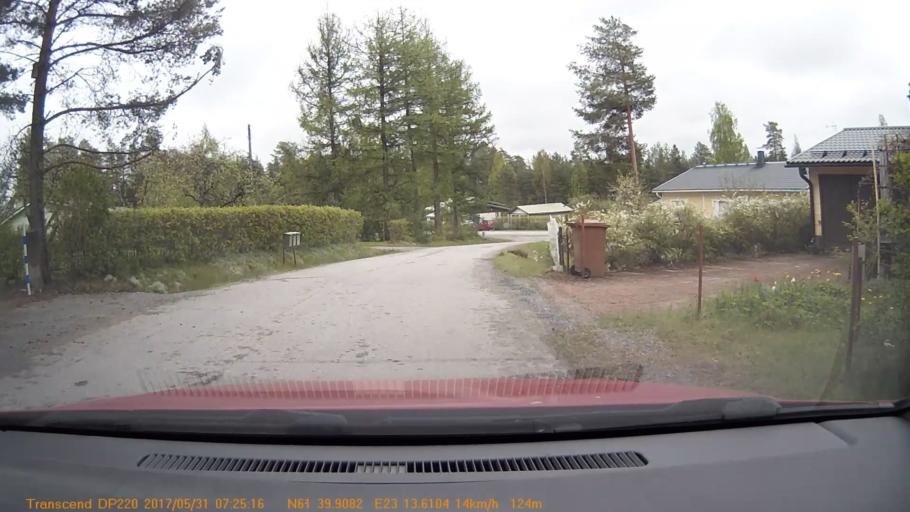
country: FI
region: Pirkanmaa
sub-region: Tampere
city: Haemeenkyroe
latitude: 61.6652
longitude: 23.2269
